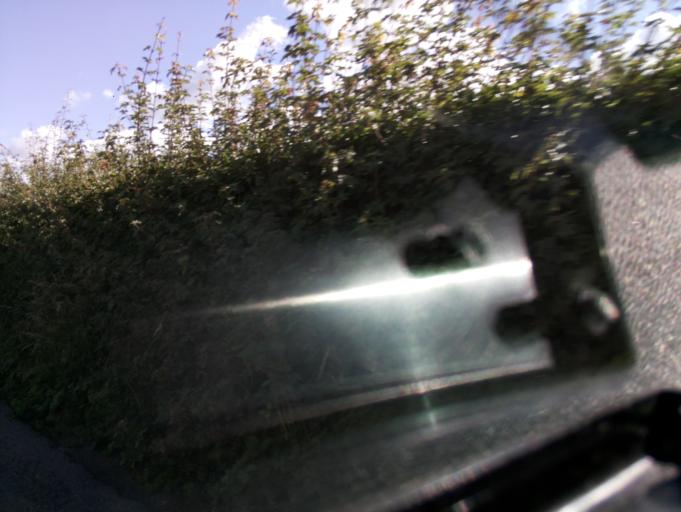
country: GB
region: England
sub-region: Gloucestershire
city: Gloucester
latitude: 51.8703
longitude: -2.3104
